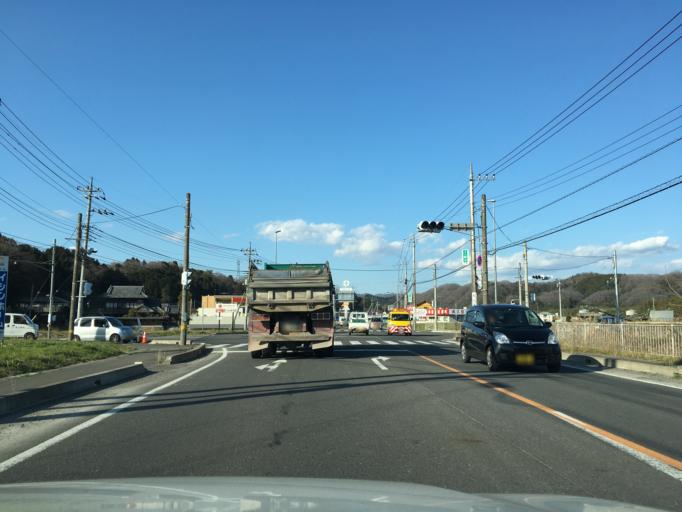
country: JP
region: Ibaraki
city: Omiya
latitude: 36.6121
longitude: 140.3984
